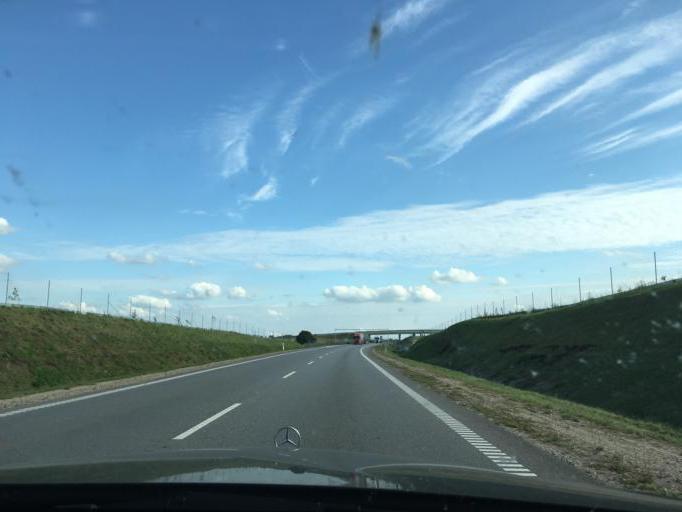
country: PL
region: Podlasie
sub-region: Powiat augustowski
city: Augustow
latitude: 53.8546
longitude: 22.9248
